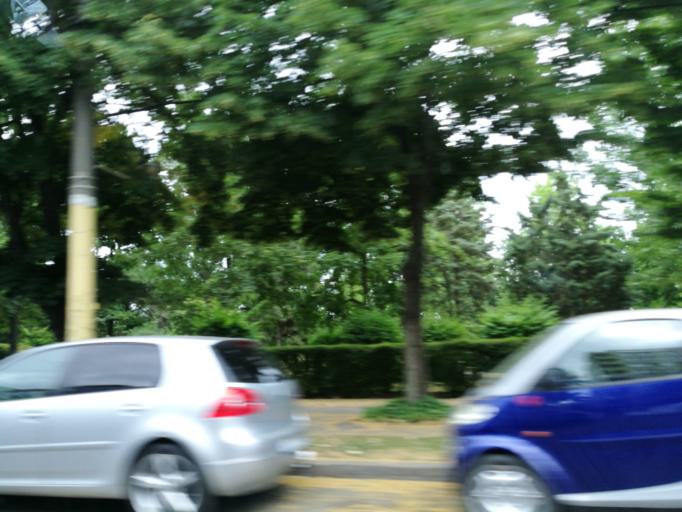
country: RO
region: Constanta
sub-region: Municipiul Constanta
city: Constanta
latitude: 44.2059
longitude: 28.6296
